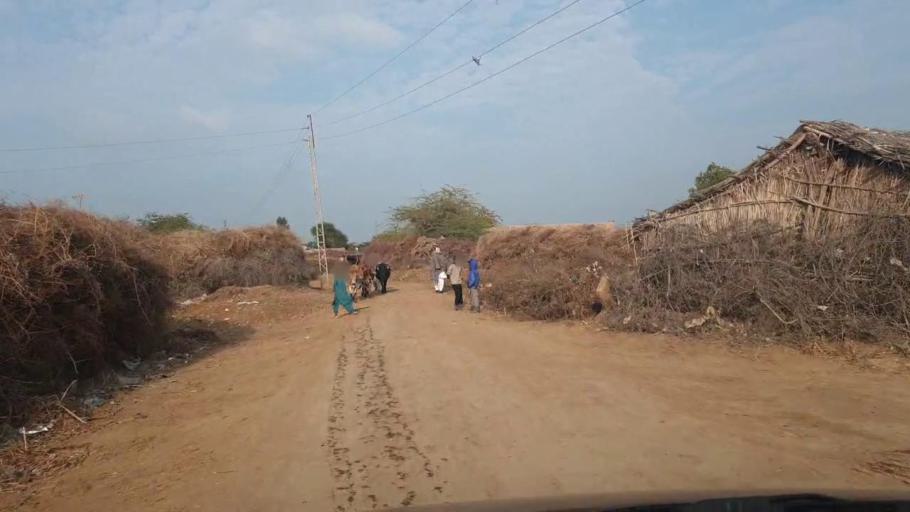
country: PK
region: Sindh
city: Shahdadpur
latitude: 25.8841
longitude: 68.7230
